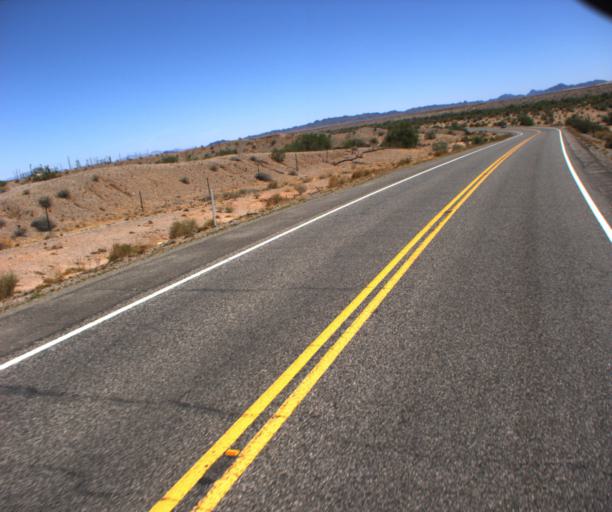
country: US
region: Arizona
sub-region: La Paz County
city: Parker
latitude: 34.0006
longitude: -114.2301
